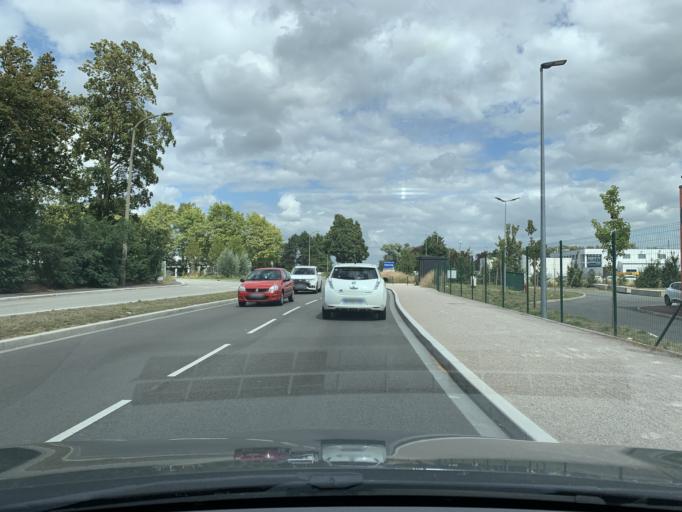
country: FR
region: Nord-Pas-de-Calais
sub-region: Departement du Pas-de-Calais
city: Henin-Beaumont
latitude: 50.4000
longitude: 2.9749
